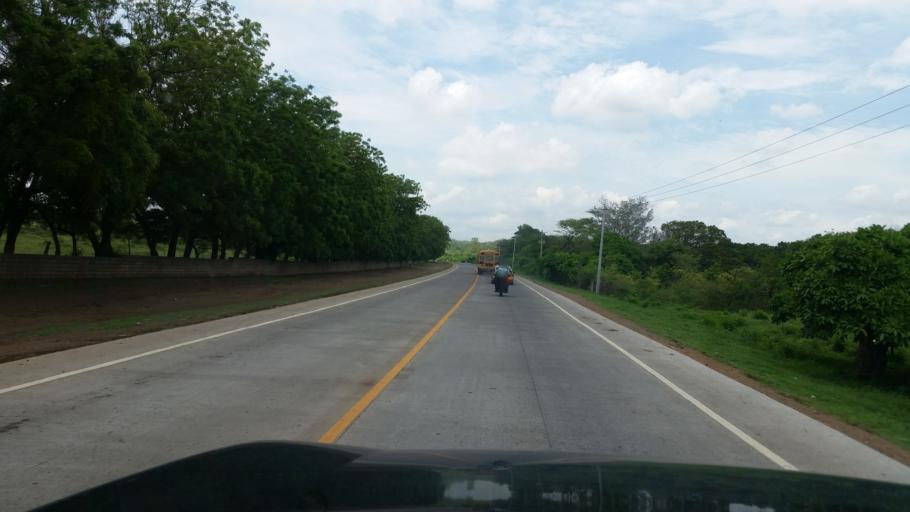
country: NI
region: Managua
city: Carlos Fonseca Amador
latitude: 12.0643
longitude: -86.4710
